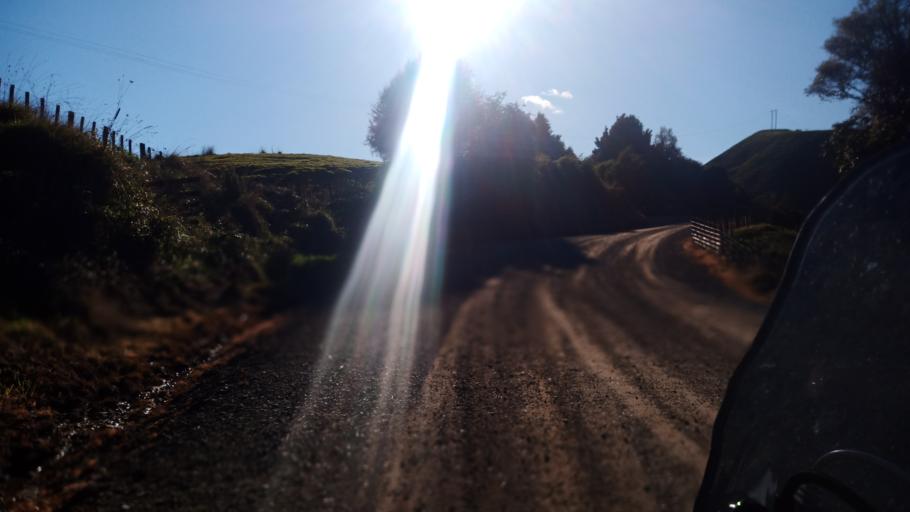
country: NZ
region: Hawke's Bay
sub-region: Wairoa District
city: Wairoa
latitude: -38.8130
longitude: 177.2901
